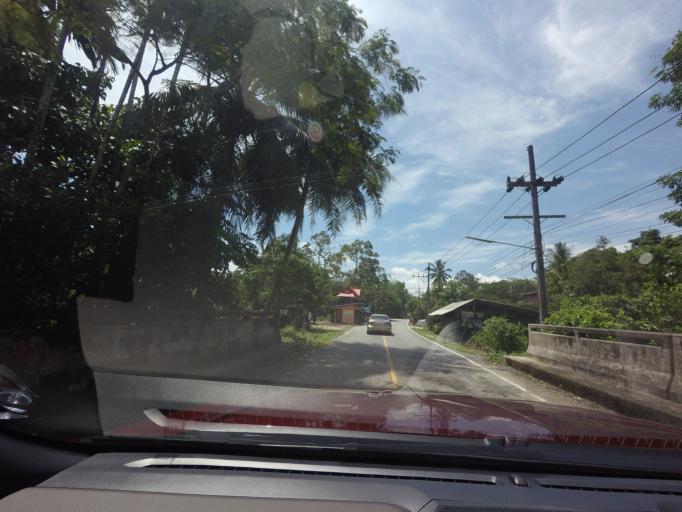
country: TH
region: Narathiwat
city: Ra-ngae
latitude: 6.2863
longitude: 101.6874
